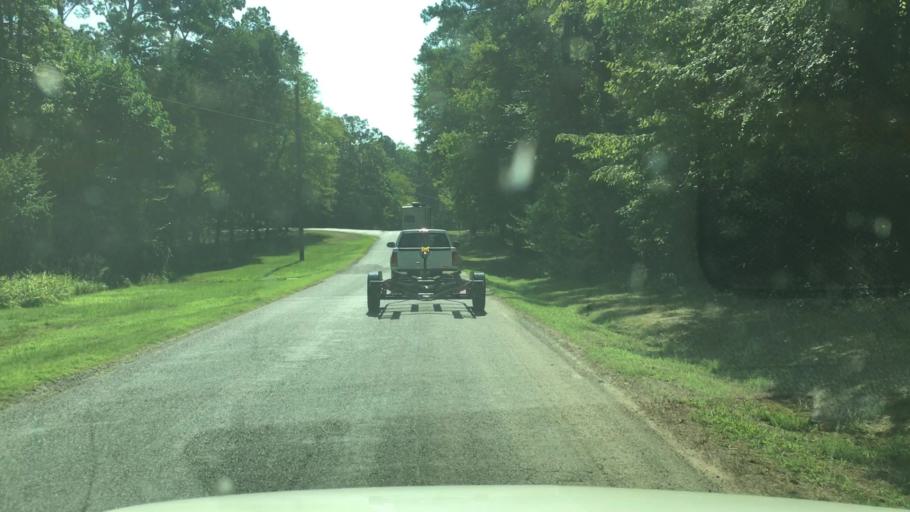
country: US
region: Arkansas
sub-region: Garland County
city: Piney
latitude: 34.5409
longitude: -93.3493
